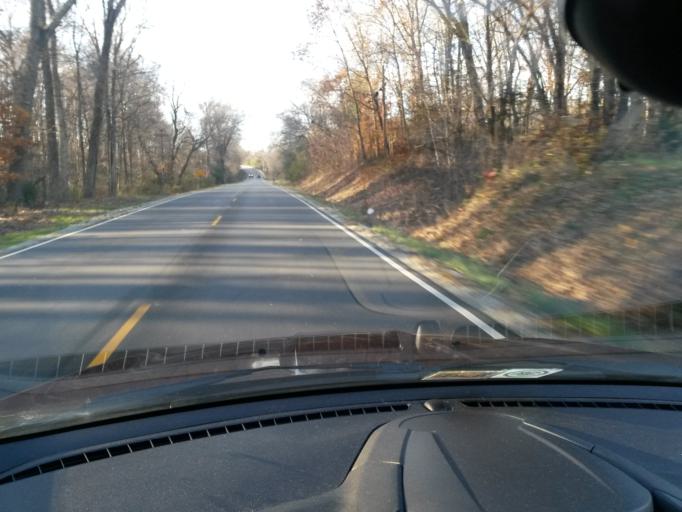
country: US
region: Virginia
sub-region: Amherst County
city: Amherst
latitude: 37.6009
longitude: -79.0639
